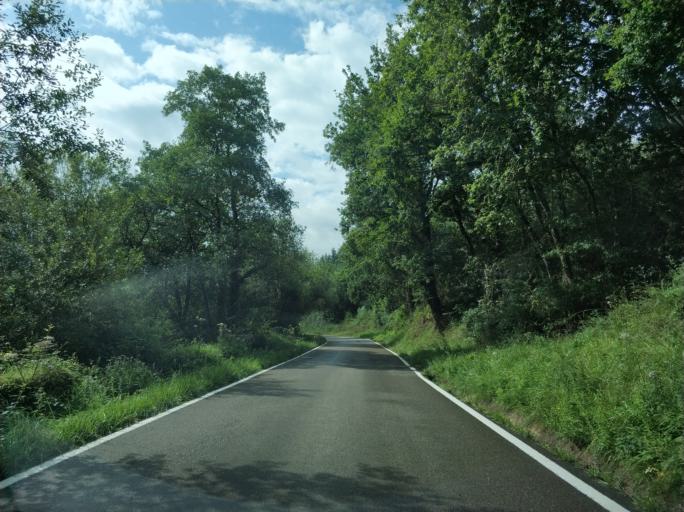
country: ES
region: Cantabria
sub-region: Provincia de Cantabria
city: Polanco
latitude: 43.3785
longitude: -3.9719
